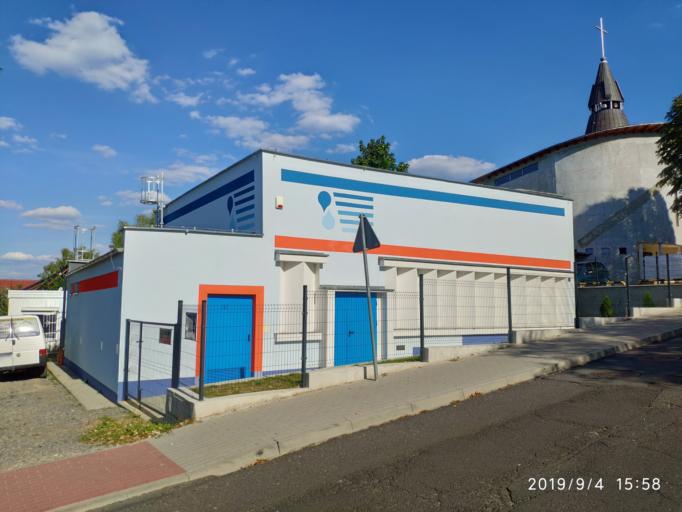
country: PL
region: Lubusz
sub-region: Zielona Gora
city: Zielona Gora
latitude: 51.9364
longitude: 15.5265
